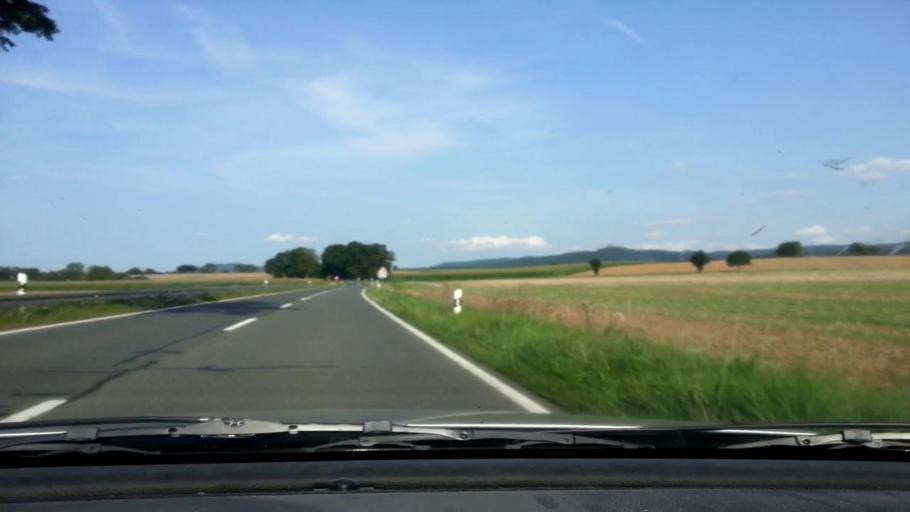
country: DE
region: Bavaria
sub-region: Upper Franconia
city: Memmelsdorf
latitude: 49.9475
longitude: 10.9880
